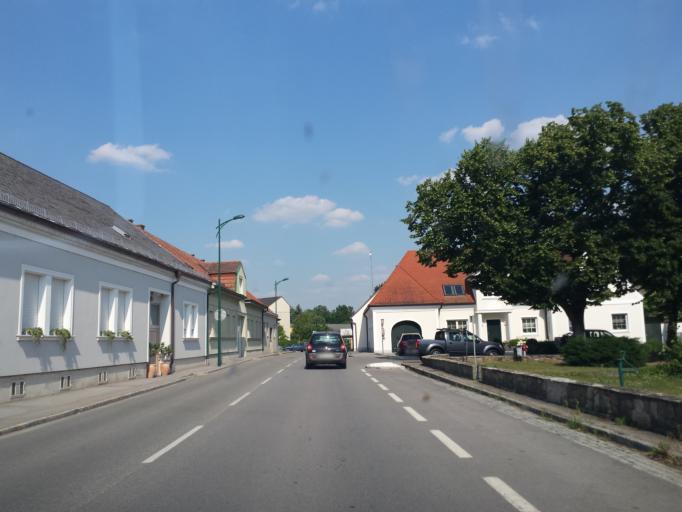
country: AT
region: Lower Austria
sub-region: Politischer Bezirk Ganserndorf
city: Aderklaa
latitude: 48.2851
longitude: 16.5383
